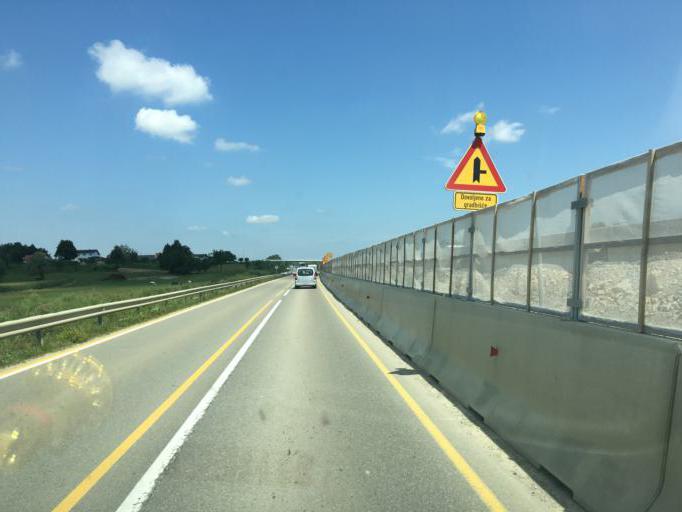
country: SI
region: Podlehnik
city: Podlehnik
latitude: 46.3543
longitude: 15.8679
